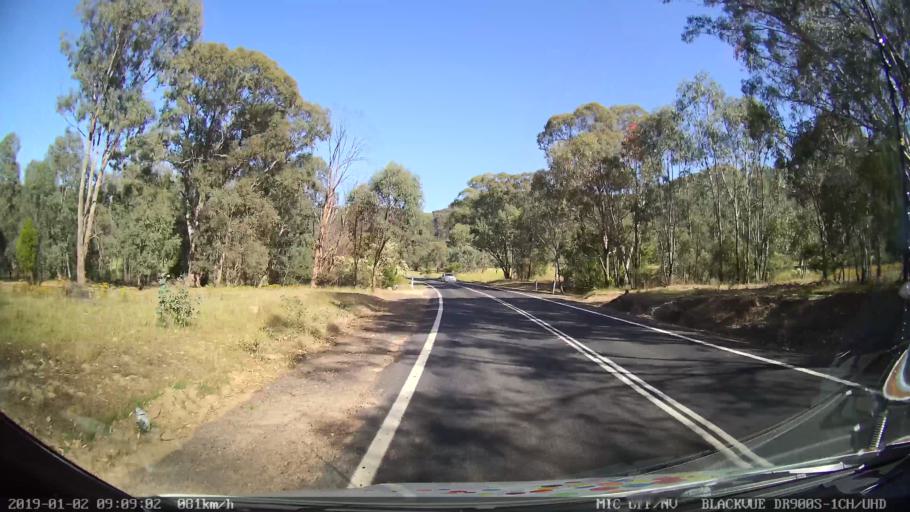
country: AU
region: New South Wales
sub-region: Tumut Shire
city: Tumut
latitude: -35.5266
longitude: 148.2853
